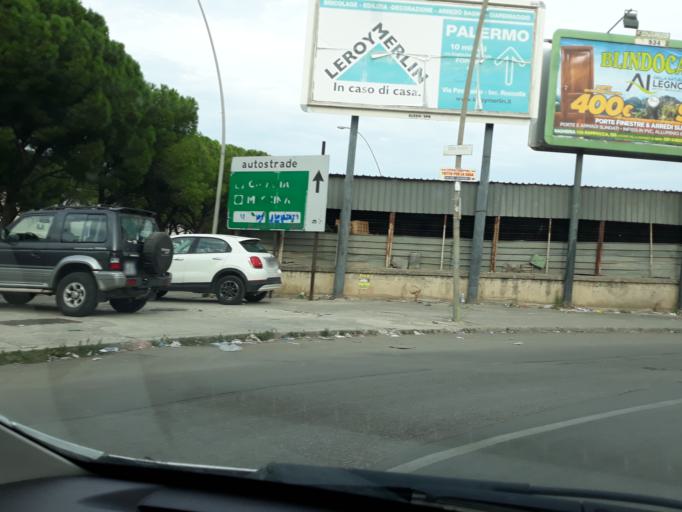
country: IT
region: Sicily
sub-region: Palermo
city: Villa Ciambra
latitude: 38.0861
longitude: 13.3521
